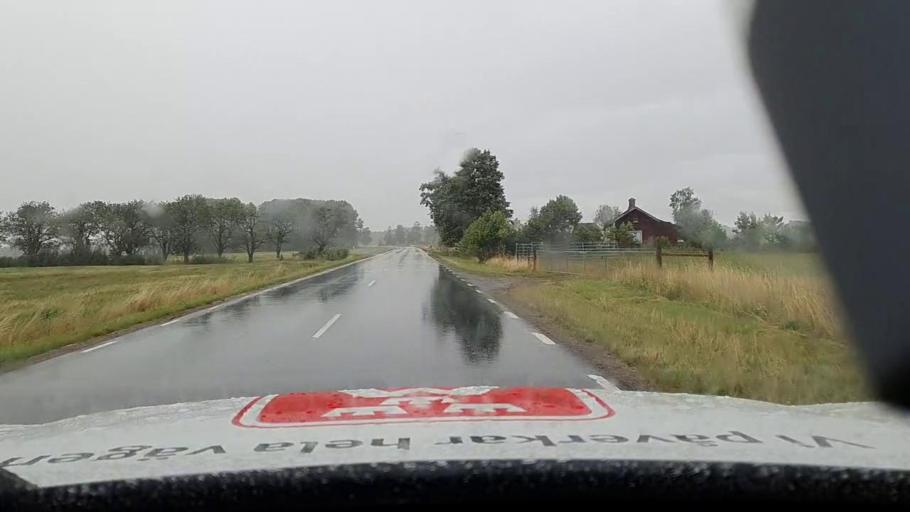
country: SE
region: Vaestra Goetaland
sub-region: Toreboda Kommun
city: Toereboda
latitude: 58.6709
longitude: 14.1332
